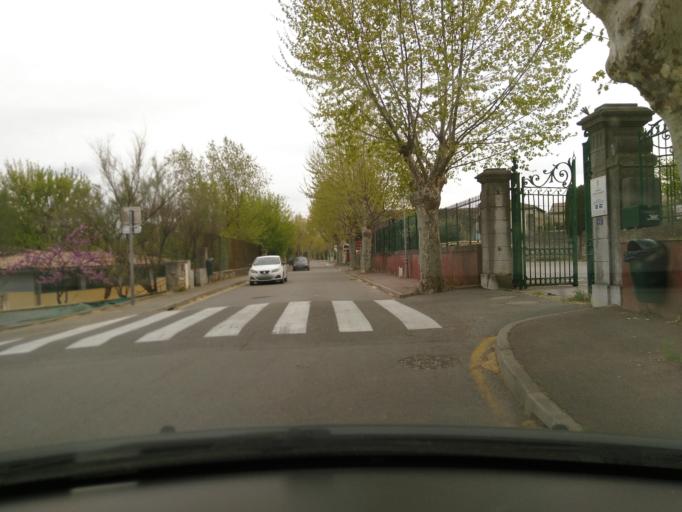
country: FR
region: Rhone-Alpes
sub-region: Departement de l'Ardeche
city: Ruoms
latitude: 44.4044
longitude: 4.3930
